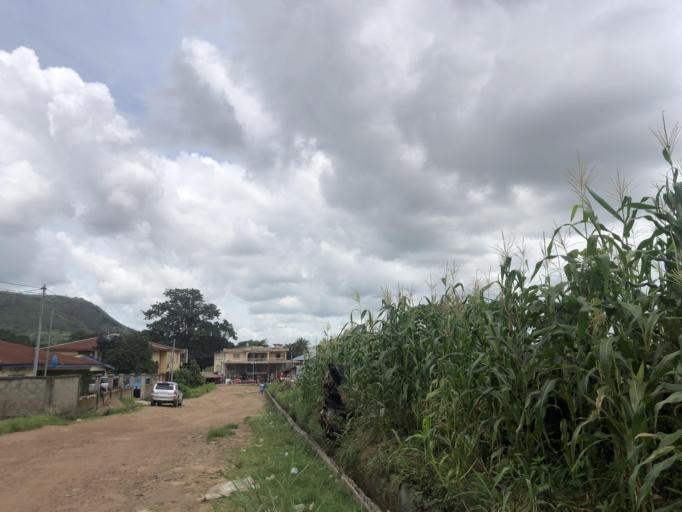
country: SL
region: Northern Province
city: Makeni
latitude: 8.8889
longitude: -12.0571
